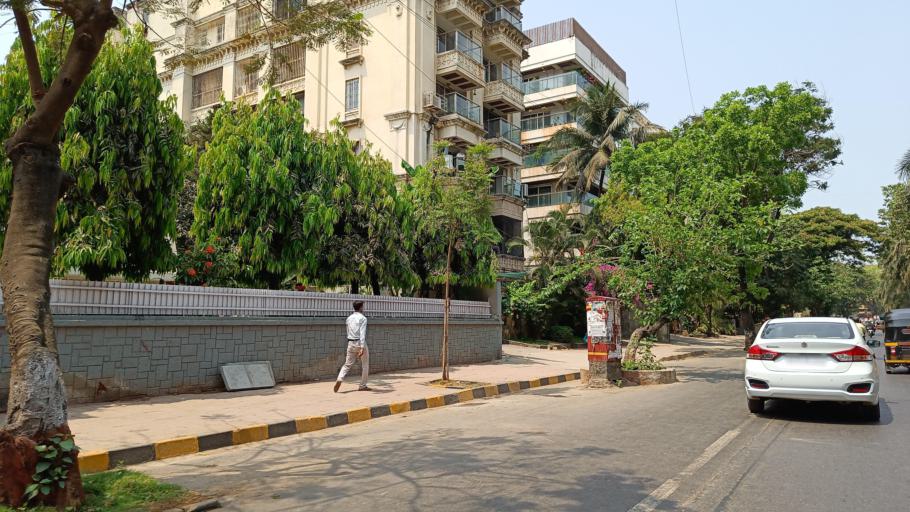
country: IN
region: Maharashtra
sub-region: Mumbai Suburban
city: Mumbai
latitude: 19.1043
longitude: 72.8290
